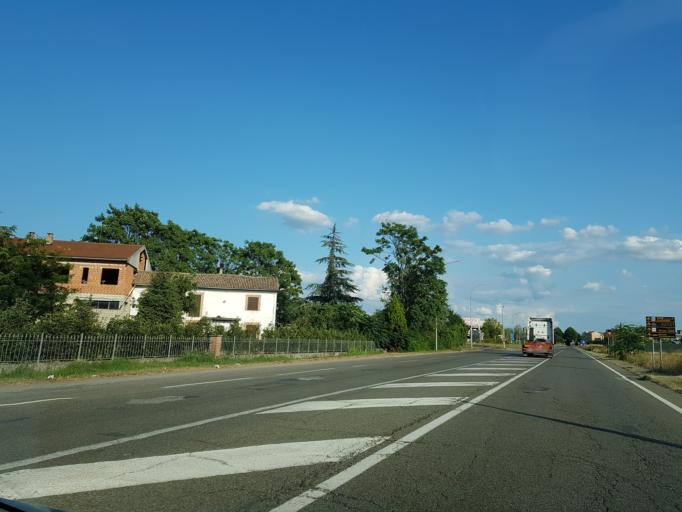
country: IT
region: Piedmont
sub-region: Provincia di Alessandria
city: Pozzolo Formigaro
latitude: 44.8017
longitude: 8.7750
